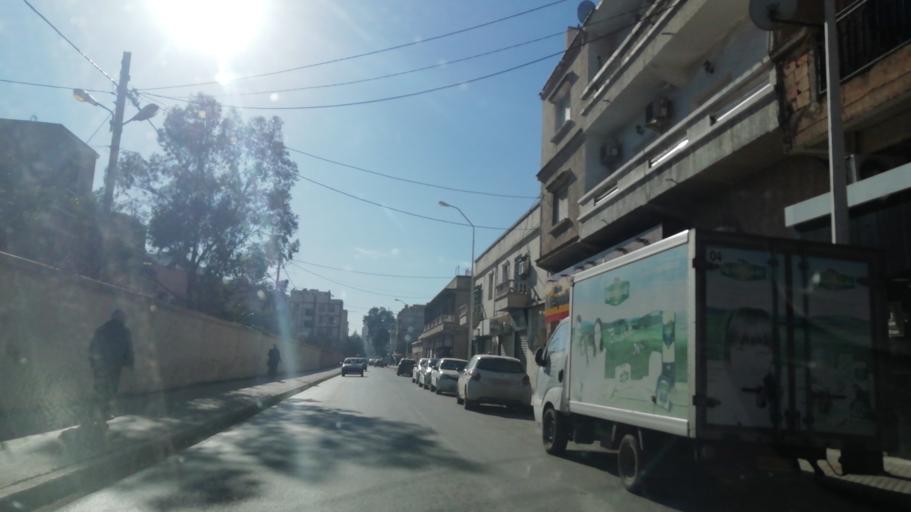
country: DZ
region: Oran
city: Oran
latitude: 35.6723
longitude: -0.6515
